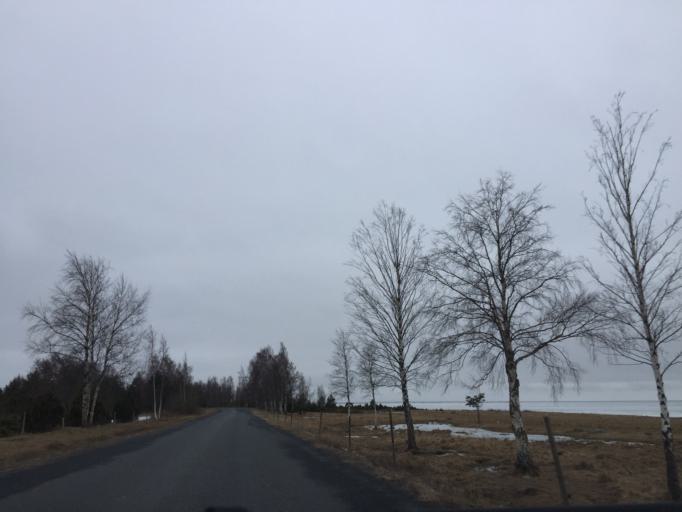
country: EE
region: Laeaene
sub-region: Haapsalu linn
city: Haapsalu
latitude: 58.7781
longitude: 23.4633
